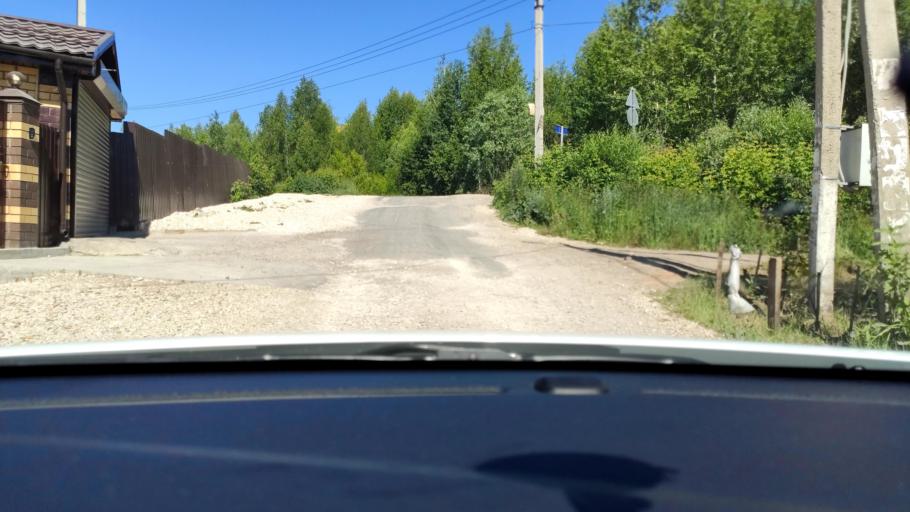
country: RU
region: Tatarstan
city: Stolbishchi
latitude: 55.7487
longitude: 49.2802
